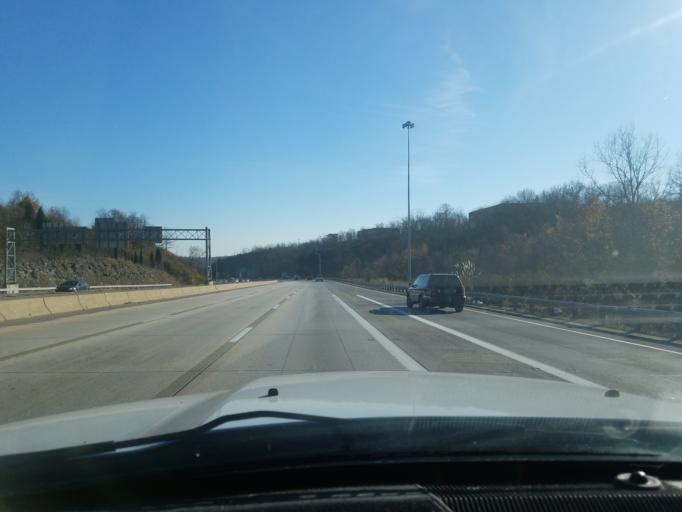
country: US
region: Kentucky
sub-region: Kenton County
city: Lakeside Park
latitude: 39.0256
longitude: -84.5634
